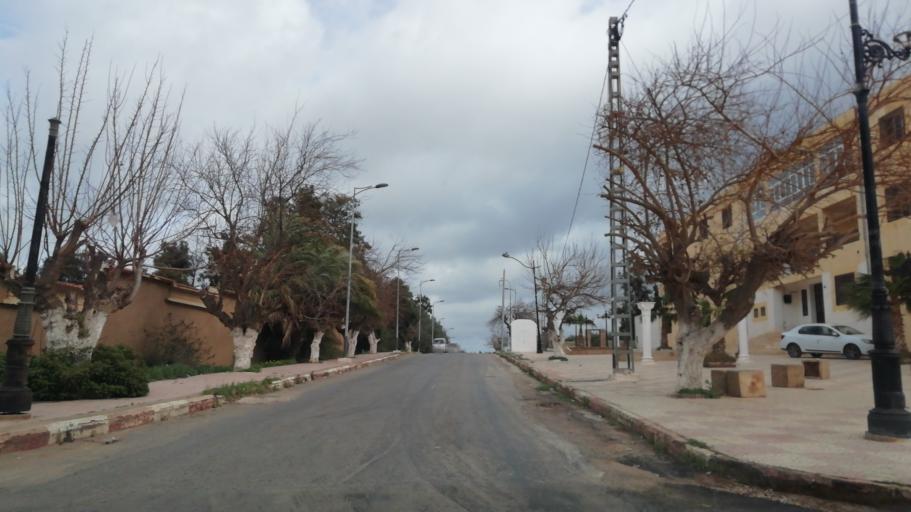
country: DZ
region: Oran
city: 'Ain el Turk
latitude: 35.6884
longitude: -0.8659
